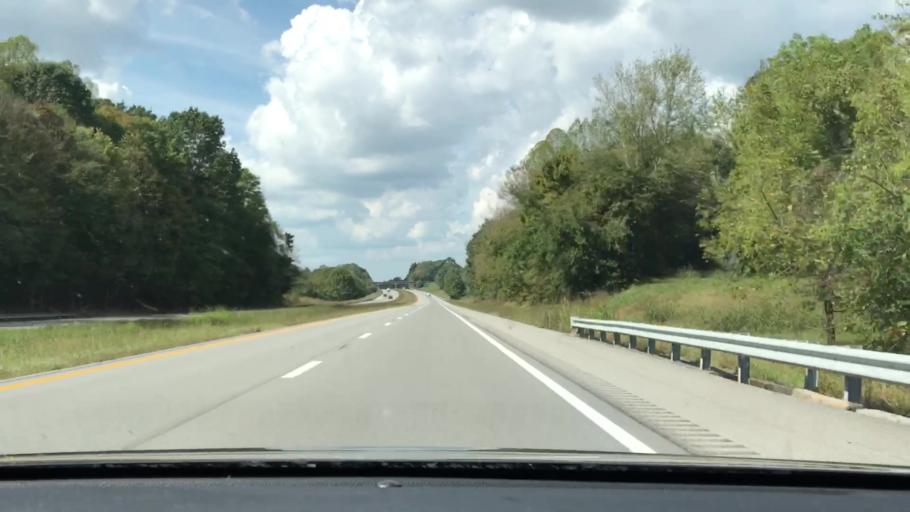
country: US
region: Kentucky
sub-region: Adair County
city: Columbia
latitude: 37.0845
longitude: -85.2567
